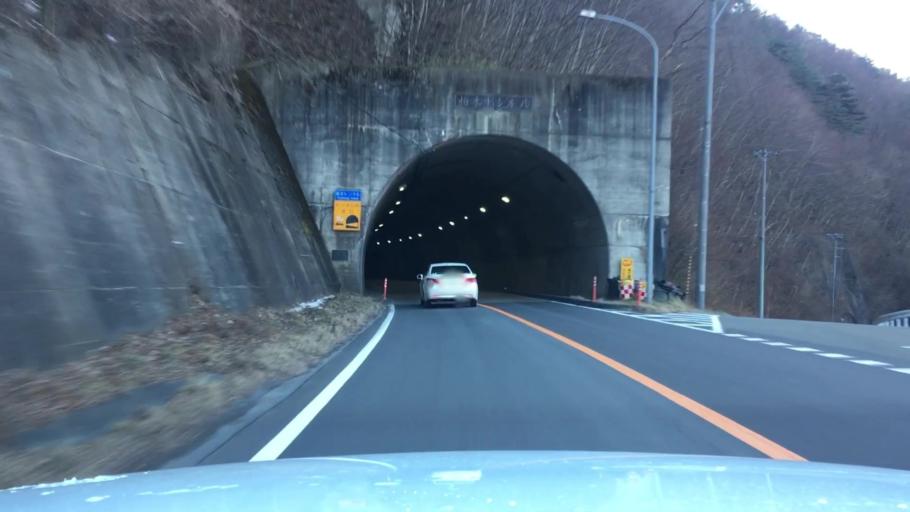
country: JP
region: Iwate
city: Tono
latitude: 39.6380
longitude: 141.6004
